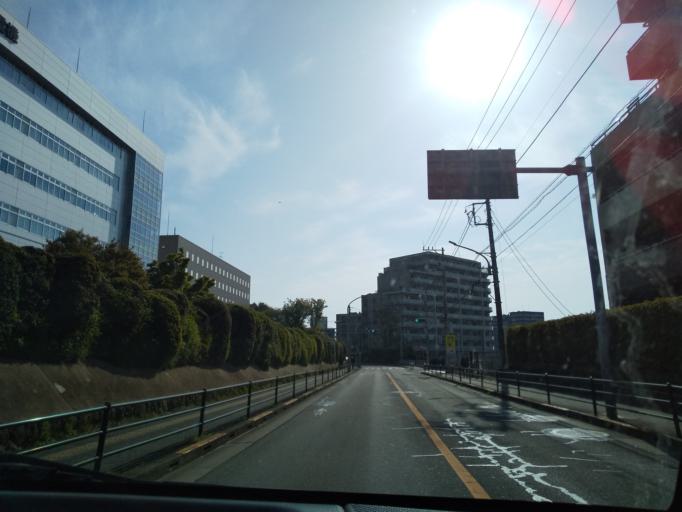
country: JP
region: Tokyo
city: Hino
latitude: 35.6585
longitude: 139.3768
